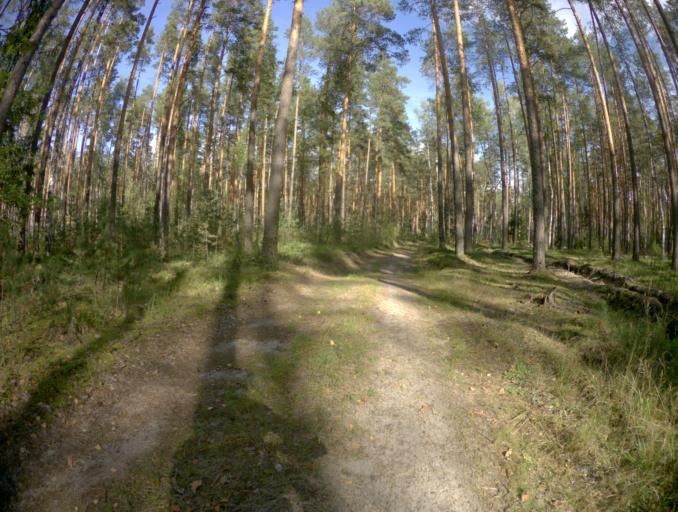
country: RU
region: Vladimir
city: Petushki
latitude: 55.8647
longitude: 39.4546
